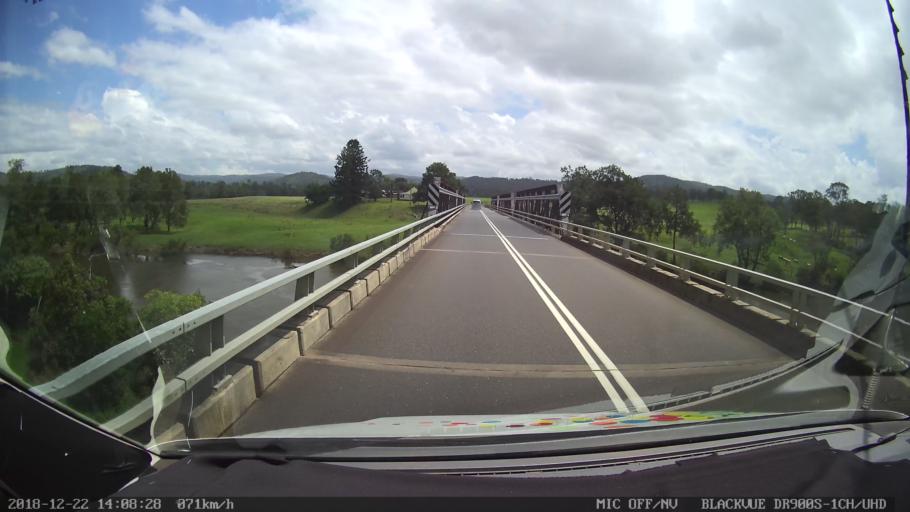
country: AU
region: New South Wales
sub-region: Clarence Valley
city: Coutts Crossing
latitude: -29.9786
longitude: 152.7253
